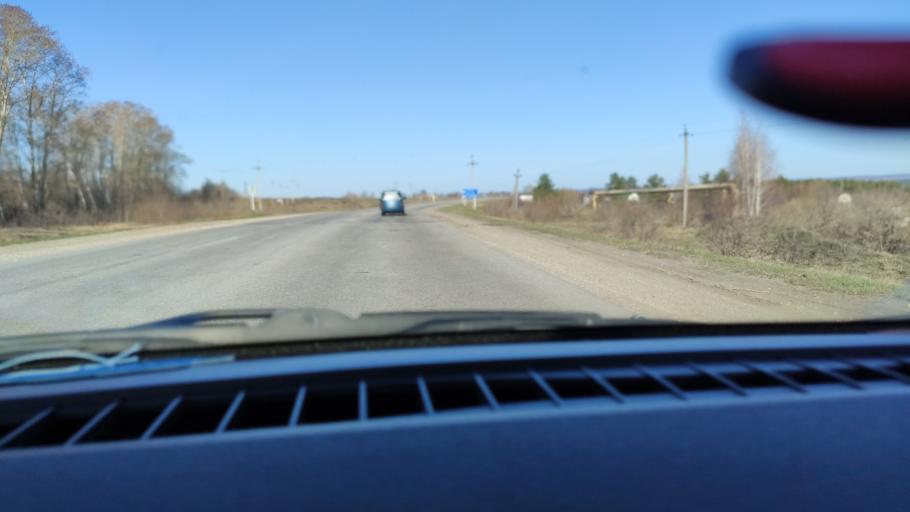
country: RU
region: Samara
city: Varlamovo
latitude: 53.1232
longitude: 48.2996
